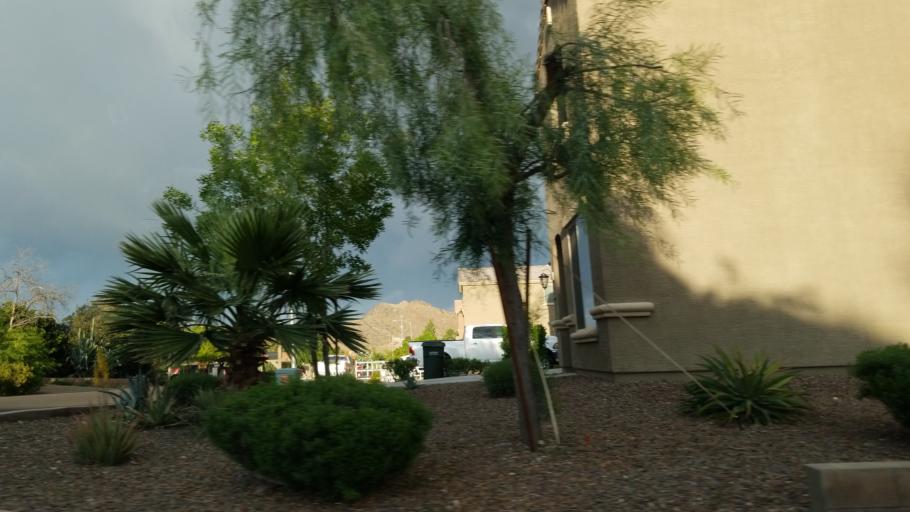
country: US
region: Arizona
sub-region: Maricopa County
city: Paradise Valley
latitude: 33.5878
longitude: -112.0565
